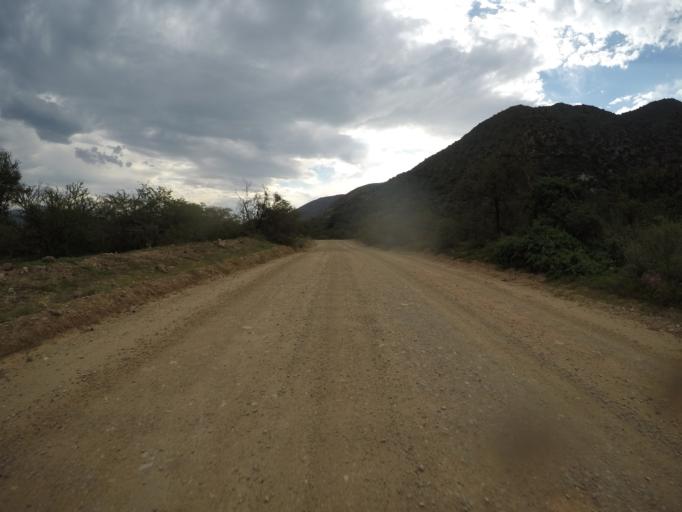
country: ZA
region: Eastern Cape
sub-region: Cacadu District Municipality
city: Kareedouw
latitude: -33.5738
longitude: 24.1359
